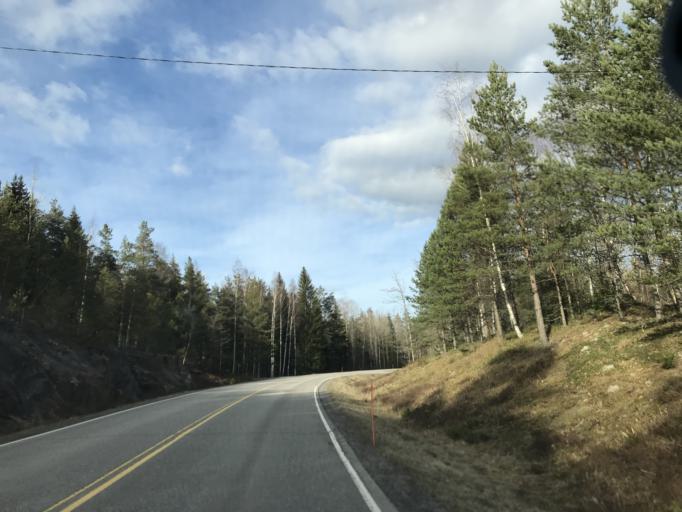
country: FI
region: Uusimaa
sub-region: Raaseporin
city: Ekenaes
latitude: 60.0788
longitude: 23.3525
